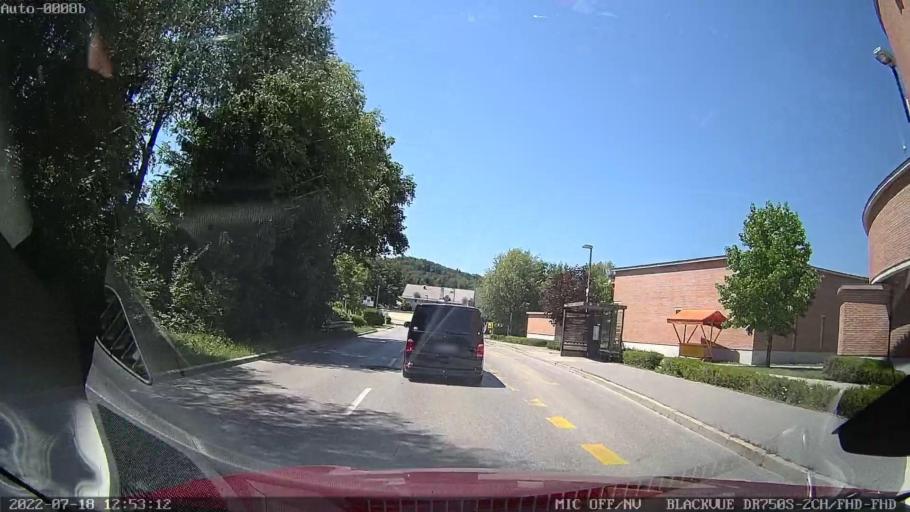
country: SI
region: Ljubljana
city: Ljubljana
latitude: 46.0740
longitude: 14.4535
